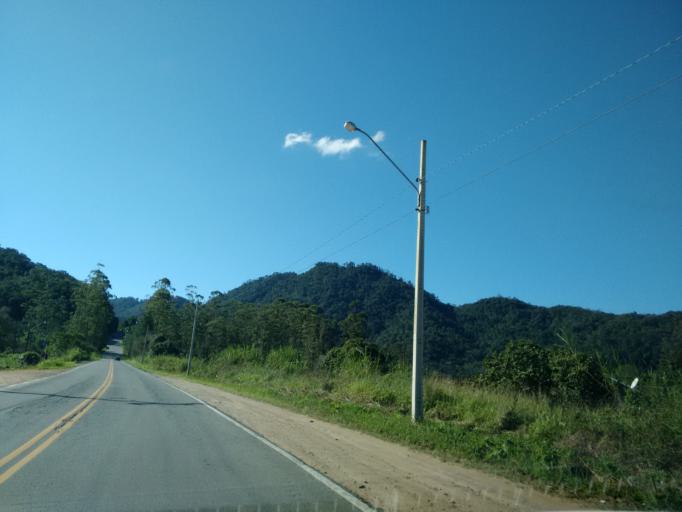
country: BR
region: Santa Catarina
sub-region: Pomerode
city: Pomerode
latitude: -26.6779
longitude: -49.1445
